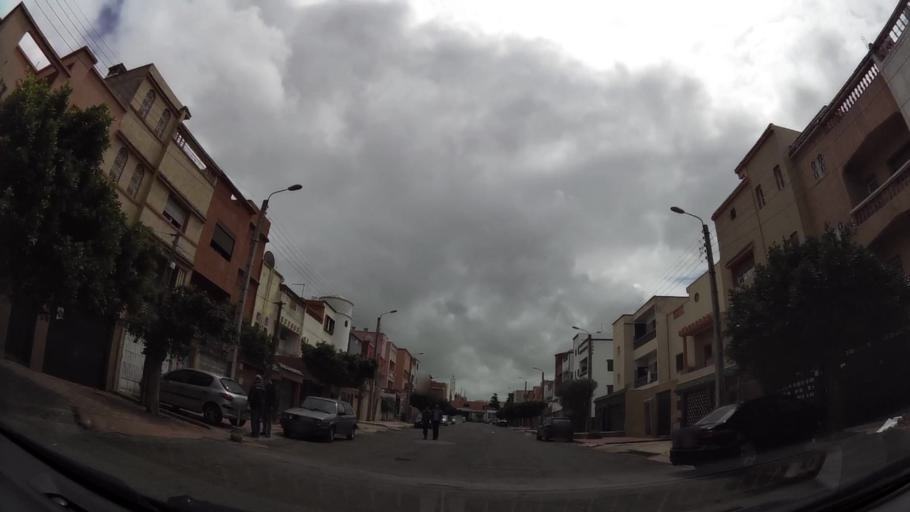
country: MA
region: Grand Casablanca
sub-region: Casablanca
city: Casablanca
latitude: 33.5385
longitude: -7.6004
